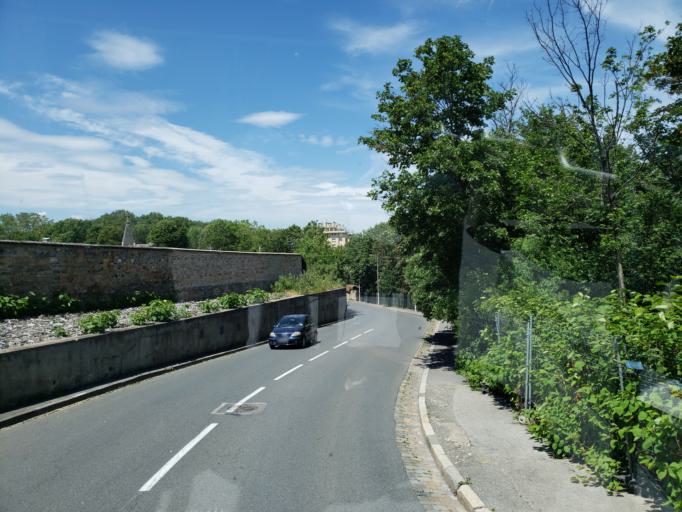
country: FR
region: Rhone-Alpes
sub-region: Departement du Rhone
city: Tassin-la-Demi-Lune
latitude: 45.7639
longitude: 4.8130
